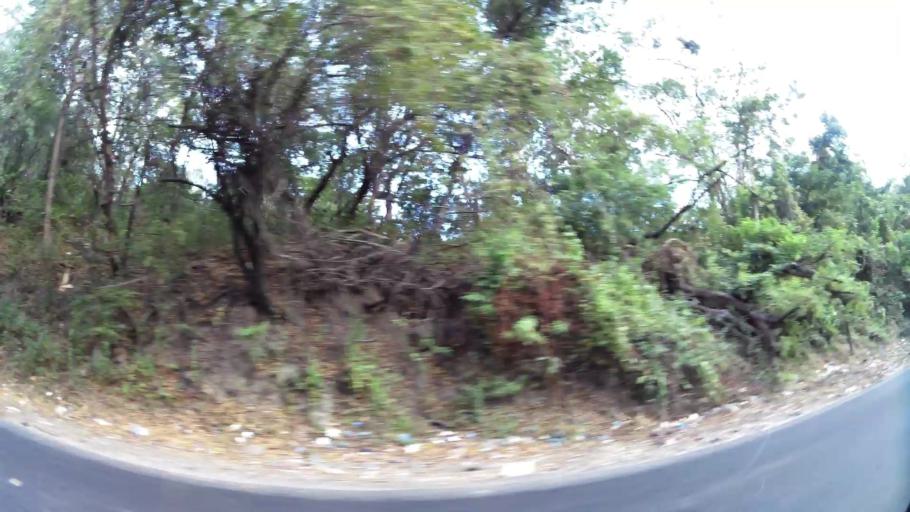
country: SV
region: San Vicente
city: Apastepeque
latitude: 13.6535
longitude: -88.7874
